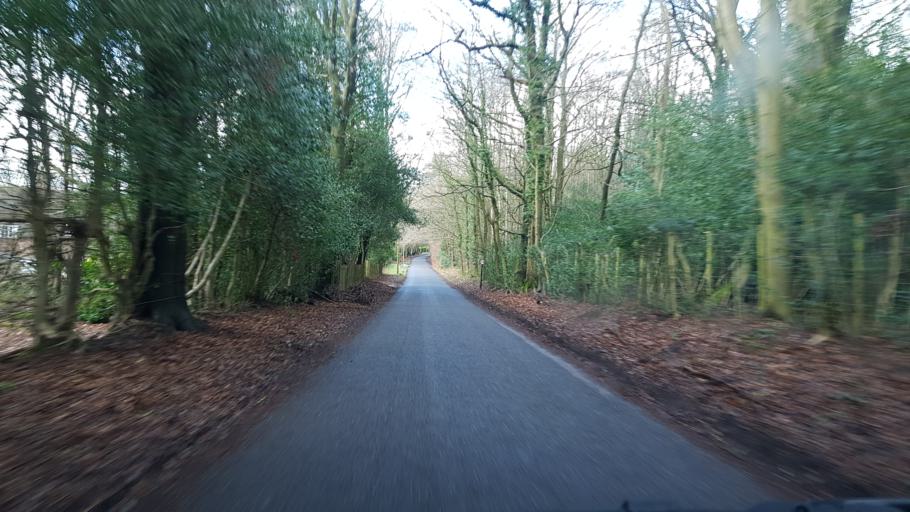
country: GB
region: England
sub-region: Surrey
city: Churt
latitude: 51.1171
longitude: -0.7762
